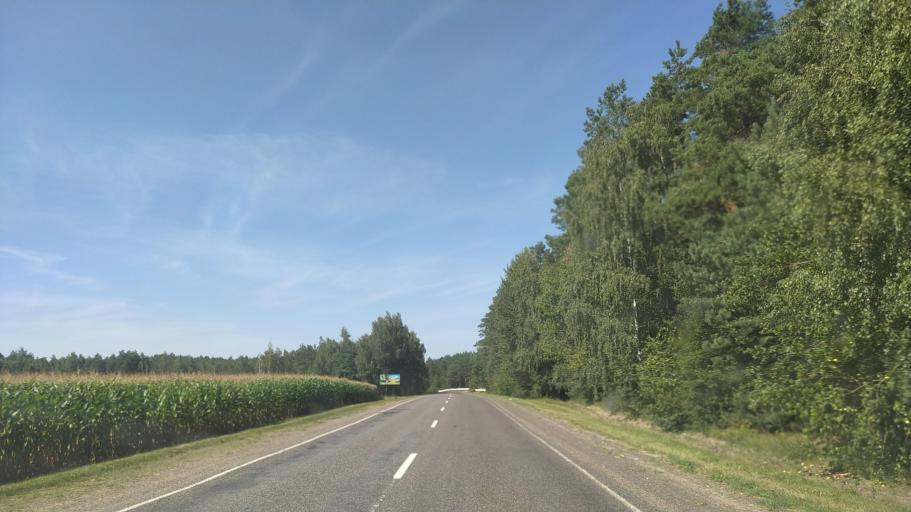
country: BY
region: Brest
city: Byaroza
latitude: 52.4032
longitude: 25.0016
